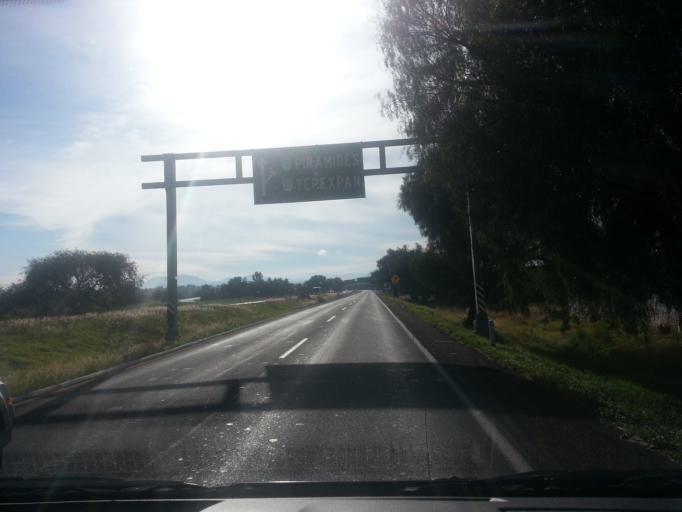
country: MX
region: Mexico
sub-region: Atenco
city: Granjas Ampliacion Santa Rosa
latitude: 19.6192
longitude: -98.9538
